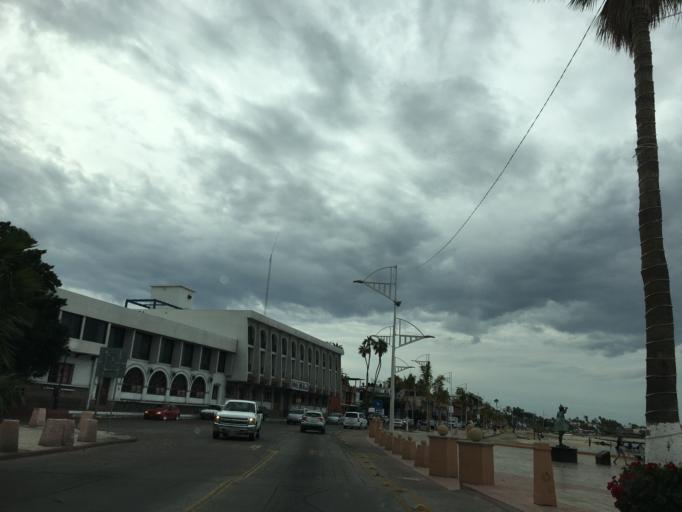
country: MX
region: Baja California Sur
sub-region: La Paz
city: La Paz
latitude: 24.1582
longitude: -110.3197
